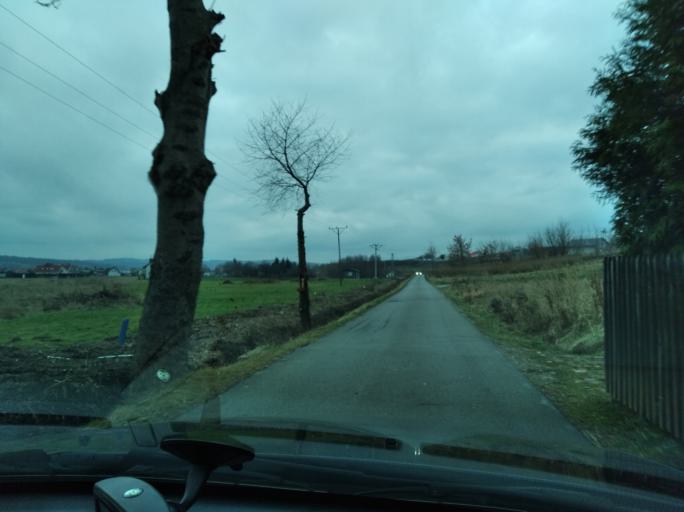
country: PL
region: Subcarpathian Voivodeship
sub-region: Powiat rzeszowski
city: Lutoryz
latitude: 49.9716
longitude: 21.9249
